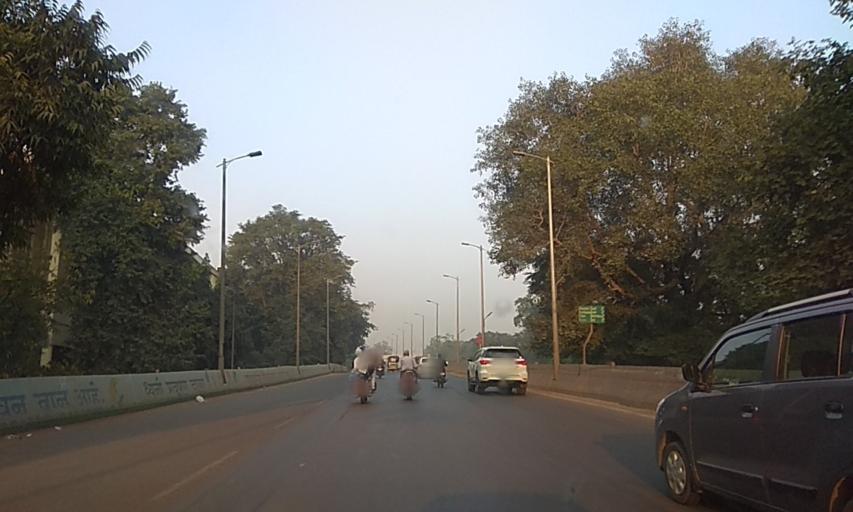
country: IN
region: Maharashtra
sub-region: Pune Division
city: Shivaji Nagar
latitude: 18.5295
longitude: 73.8579
